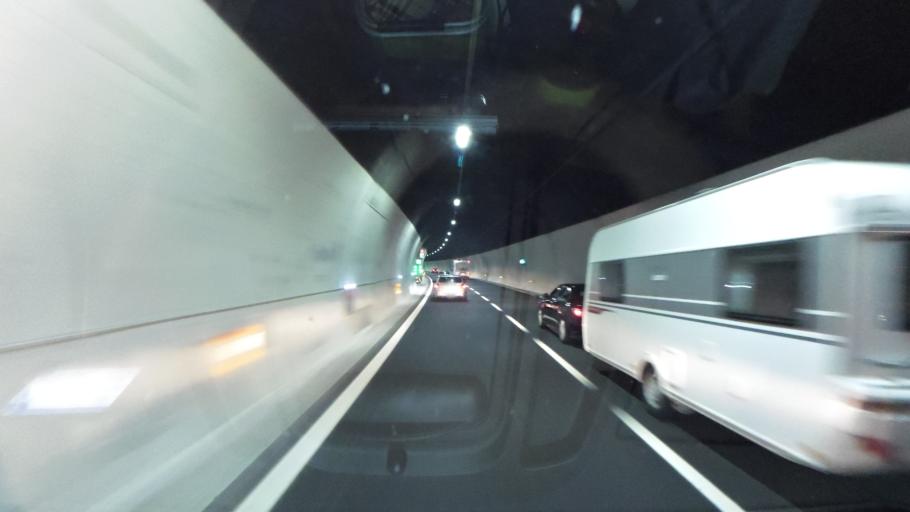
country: IT
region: Friuli Venezia Giulia
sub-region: Provincia di Udine
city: Moggio di Sotto
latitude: 46.3951
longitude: 13.1839
